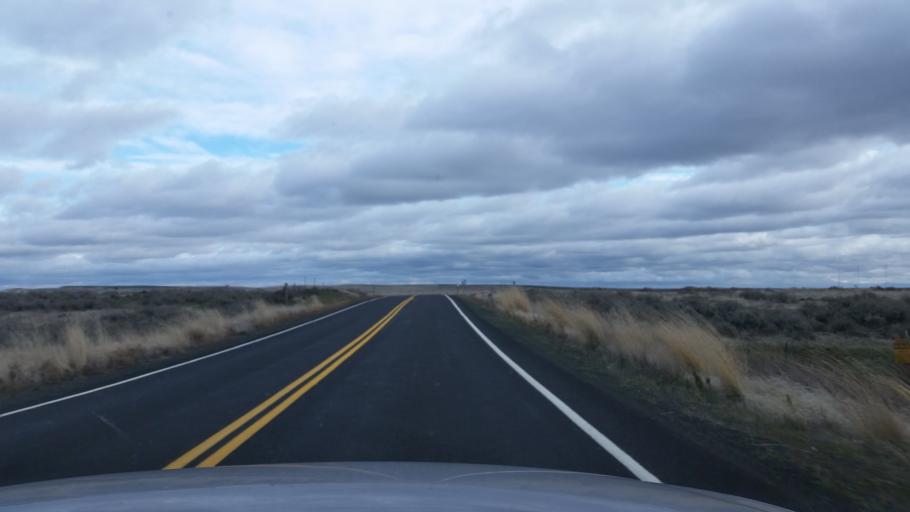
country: US
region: Washington
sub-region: Lincoln County
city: Davenport
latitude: 47.3339
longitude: -117.9934
